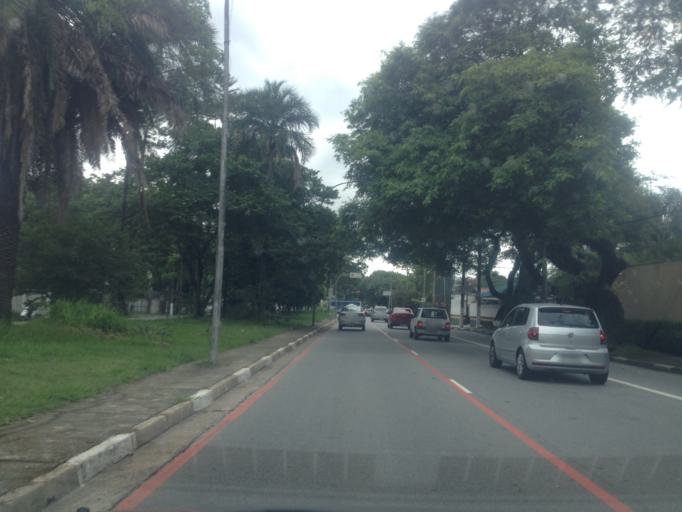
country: BR
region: Sao Paulo
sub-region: Sao Paulo
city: Sao Paulo
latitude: -23.5663
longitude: -46.7101
